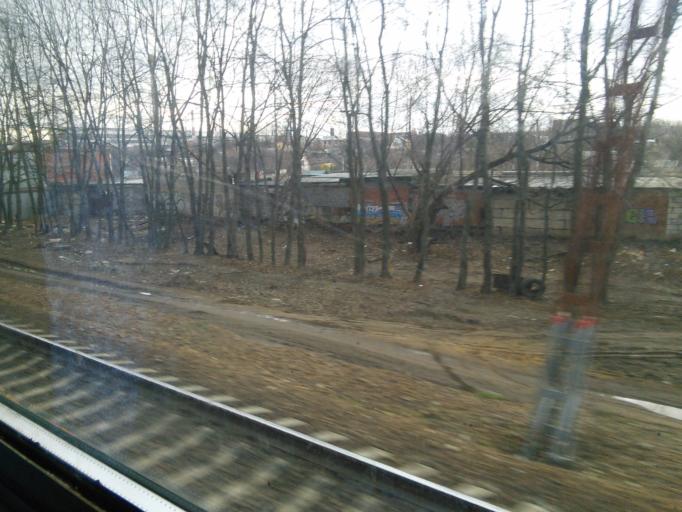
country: RU
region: Moskovskaya
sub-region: Podol'skiy Rayon
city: Podol'sk
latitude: 55.4139
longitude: 37.5554
